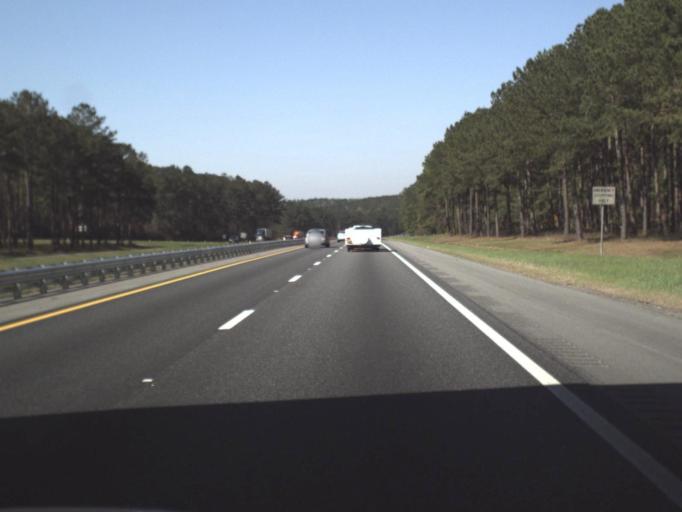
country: US
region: Florida
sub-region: Gadsden County
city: Chattahoochee
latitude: 30.6181
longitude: -84.8224
